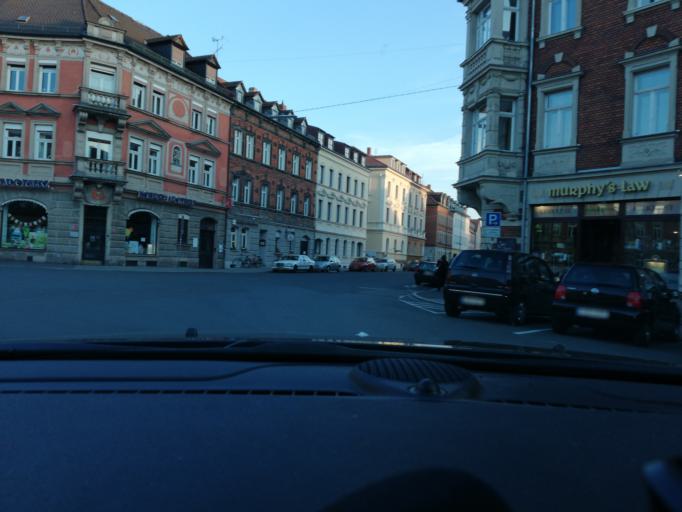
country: DE
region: Bavaria
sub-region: Regierungsbezirk Mittelfranken
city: Erlangen
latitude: 49.5981
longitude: 11.0145
